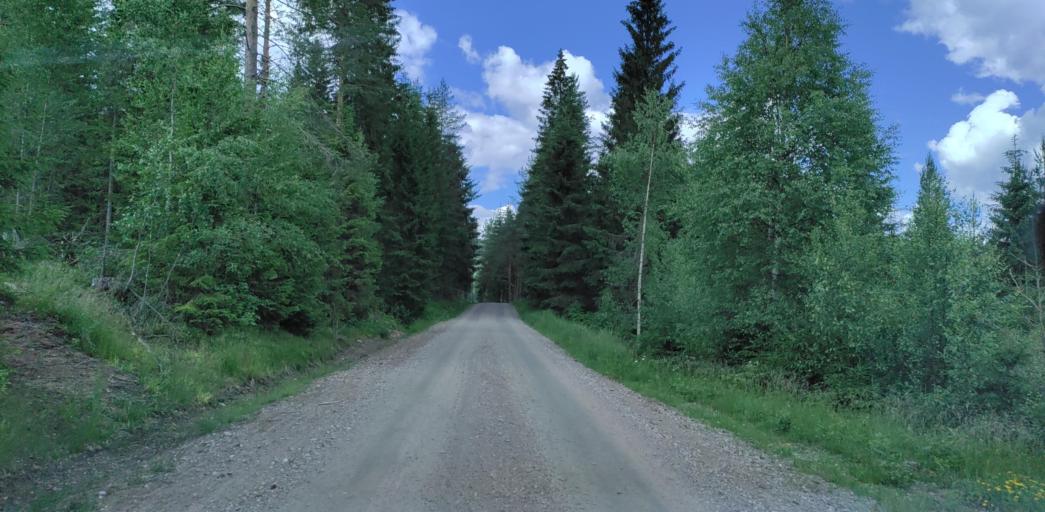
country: SE
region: Vaermland
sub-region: Hagfors Kommun
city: Ekshaerad
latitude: 60.1008
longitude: 13.3690
